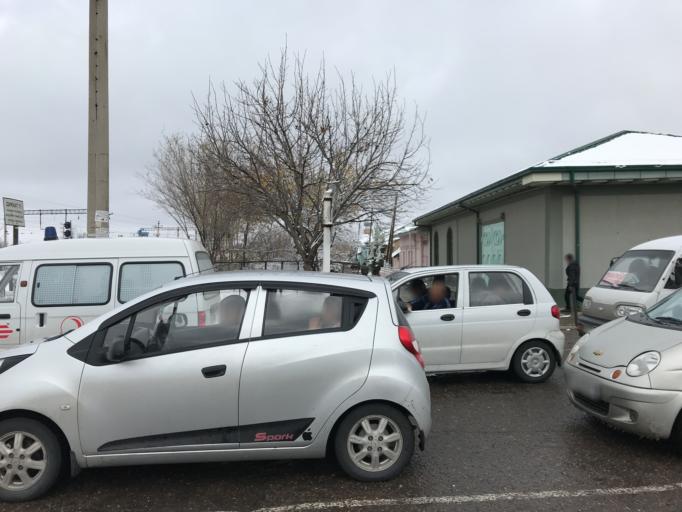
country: UZ
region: Toshkent
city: Yangiyul
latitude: 41.1084
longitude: 69.0546
